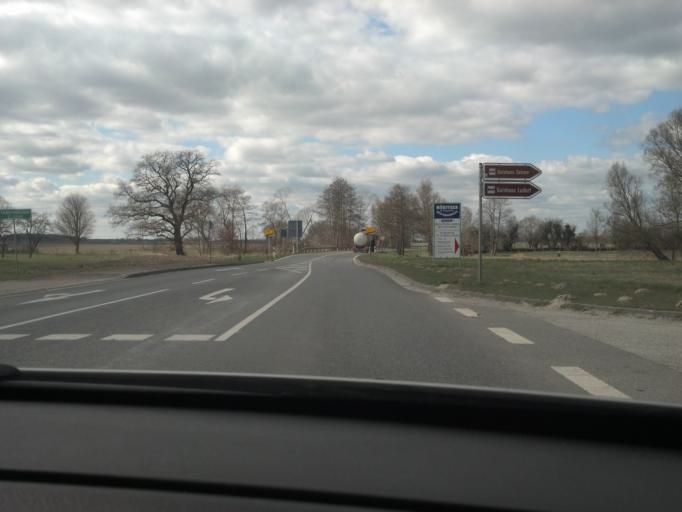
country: DE
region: Mecklenburg-Vorpommern
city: Rechlin
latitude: 53.3264
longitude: 12.6887
